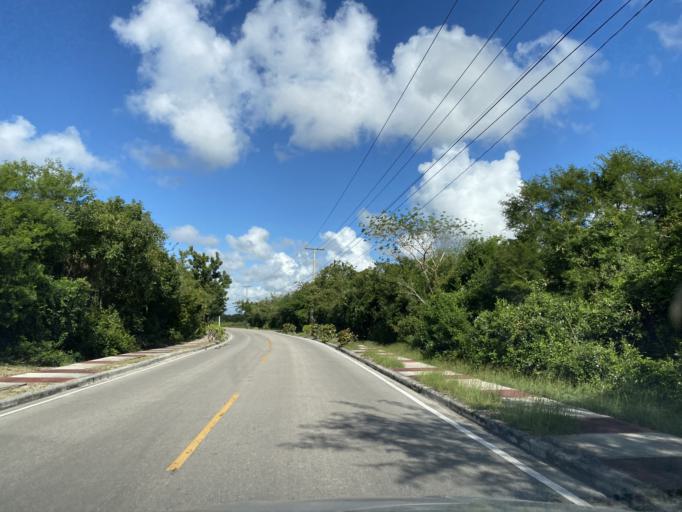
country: DO
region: La Altagracia
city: San Rafael del Yuma
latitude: 18.3411
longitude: -68.8127
